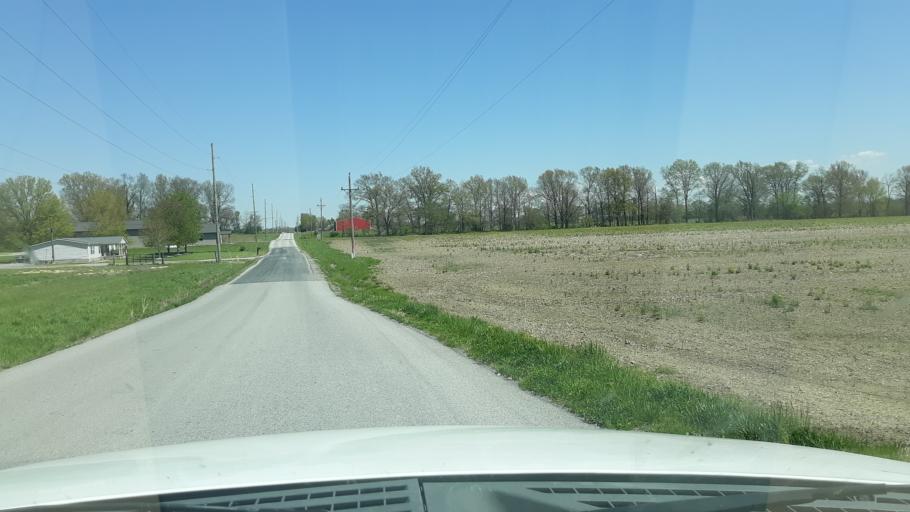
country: US
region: Illinois
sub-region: Saline County
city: Harrisburg
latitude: 37.8342
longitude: -88.6515
